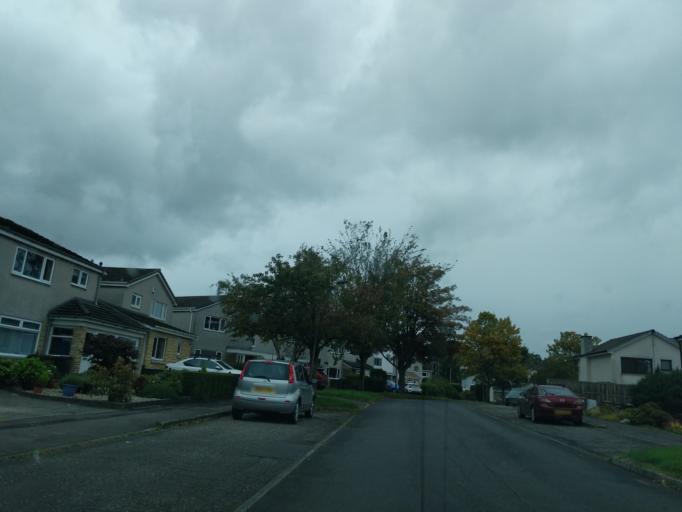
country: GB
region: Scotland
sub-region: Edinburgh
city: Balerno
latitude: 55.8781
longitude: -3.3460
